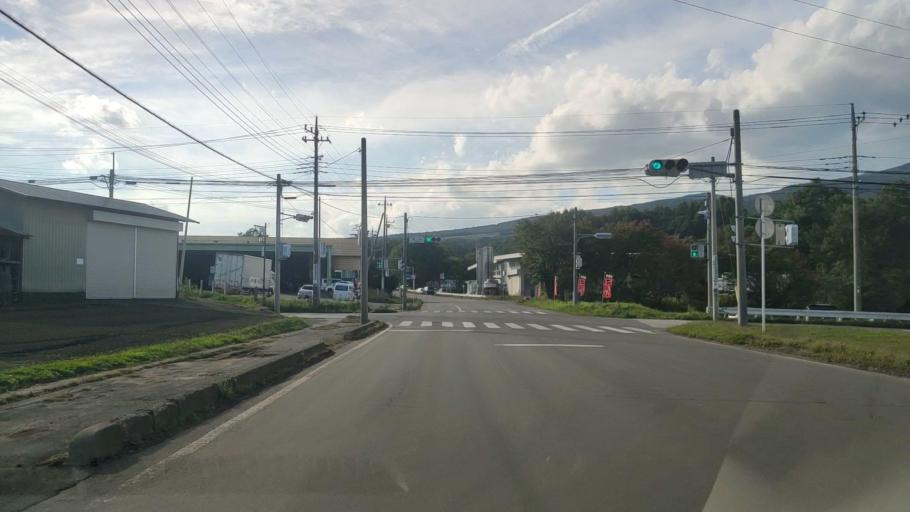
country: JP
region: Nagano
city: Komoro
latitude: 36.4864
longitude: 138.4512
